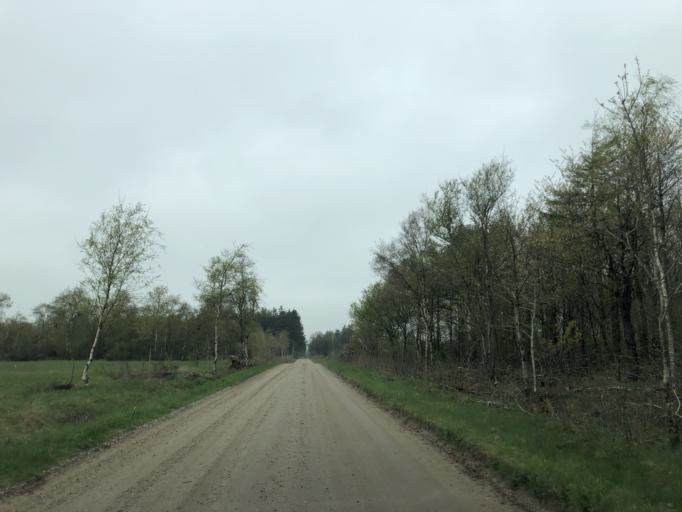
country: DK
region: Central Jutland
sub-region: Lemvig Kommune
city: Lemvig
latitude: 56.5036
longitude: 8.3280
